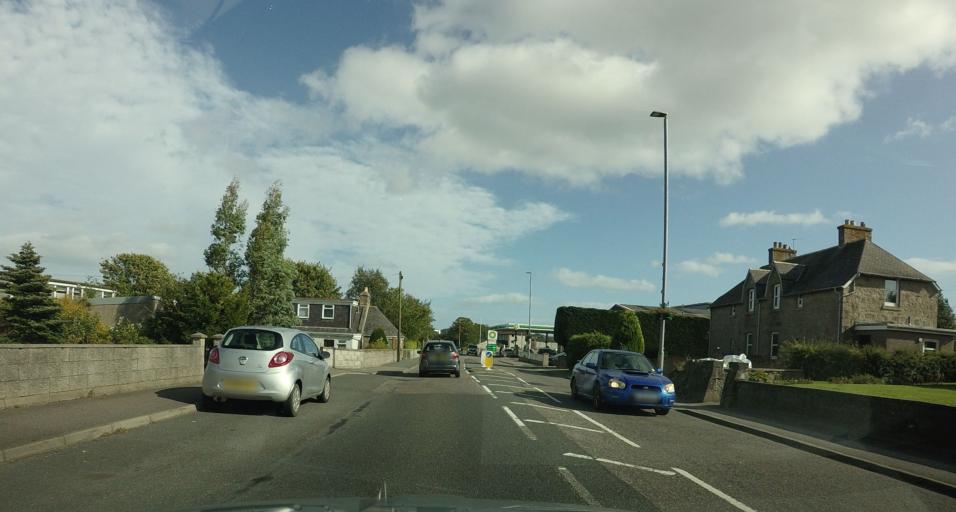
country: GB
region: Scotland
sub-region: Aberdeenshire
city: Westhill
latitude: 57.1498
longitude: -2.2972
